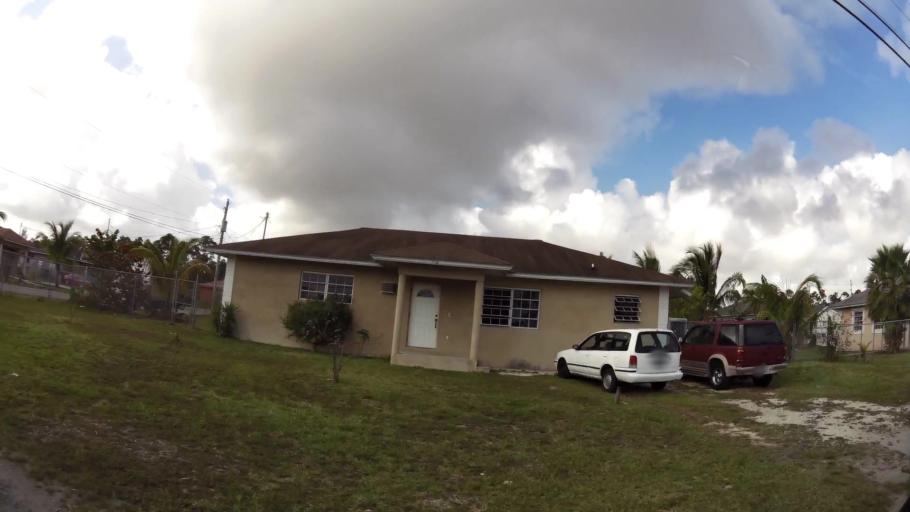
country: BS
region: Freeport
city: Freeport
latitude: 26.5266
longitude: -78.7111
